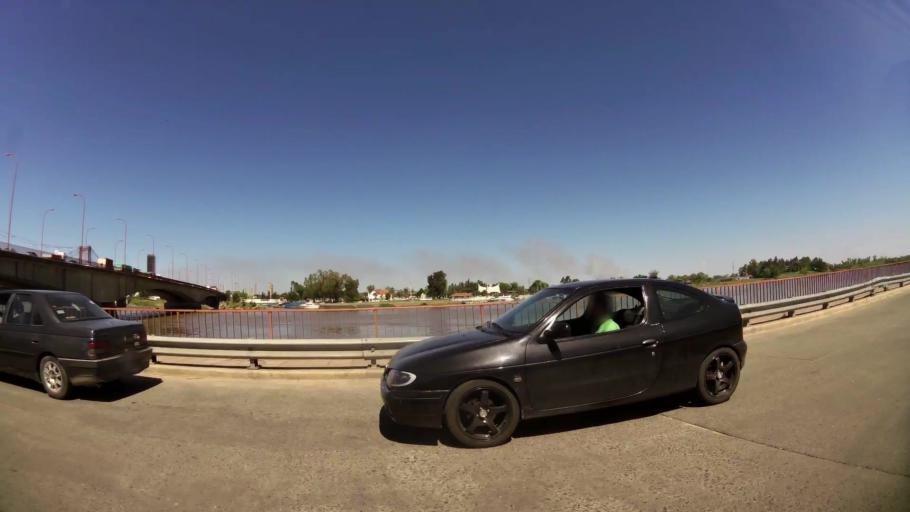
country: AR
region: Santa Fe
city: Santa Fe de la Vera Cruz
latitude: -31.6409
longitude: -60.6834
